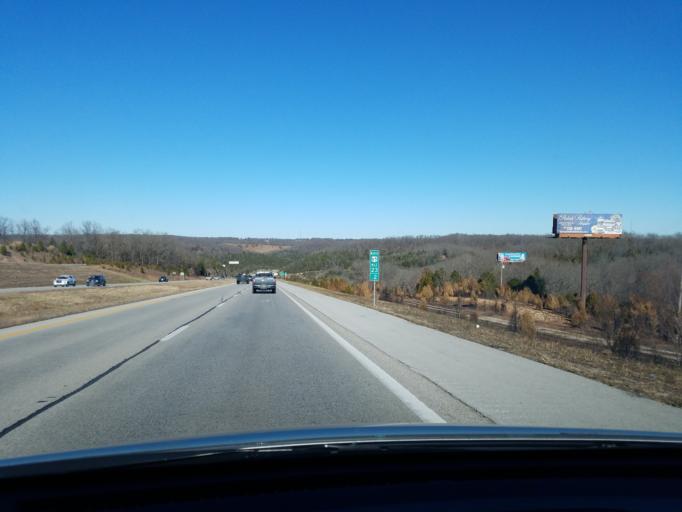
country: US
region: Missouri
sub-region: Taney County
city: Merriam Woods
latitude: 36.8130
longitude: -93.2255
